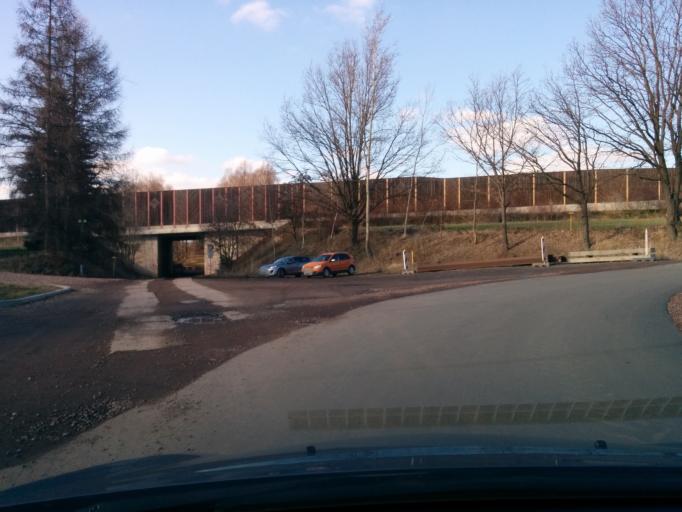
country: DE
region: Saxony
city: Neukirchen
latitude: 50.7899
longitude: 12.8394
